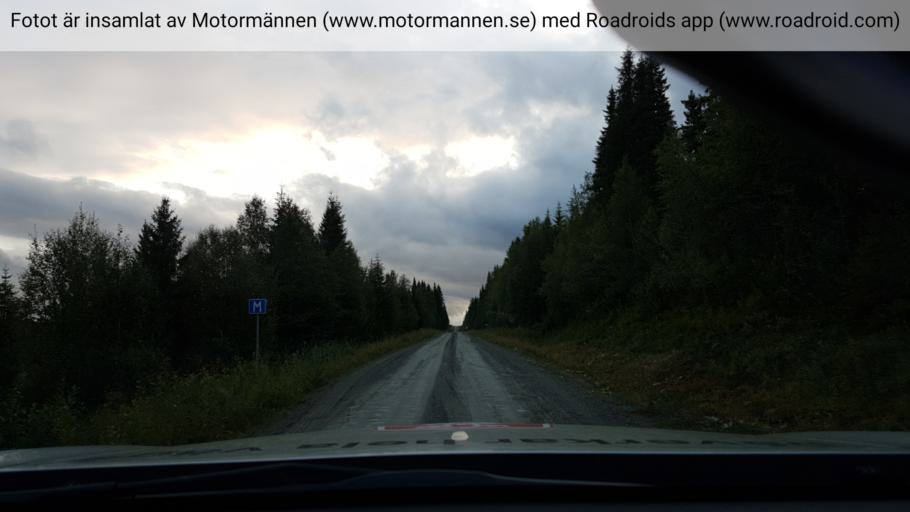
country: SE
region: Vaesterbotten
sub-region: Vilhelmina Kommun
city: Sjoberg
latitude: 65.4961
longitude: 15.5265
